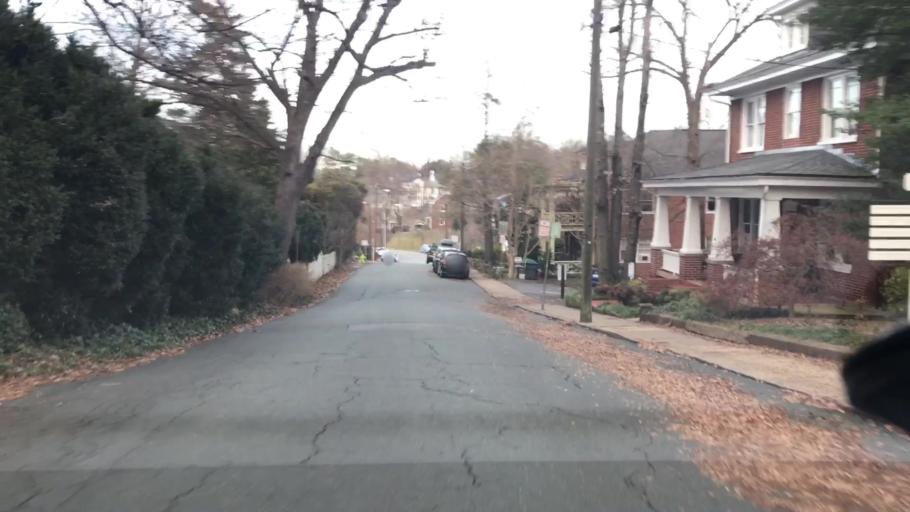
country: US
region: Virginia
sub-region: City of Charlottesville
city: Charlottesville
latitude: 38.0332
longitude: -78.4786
